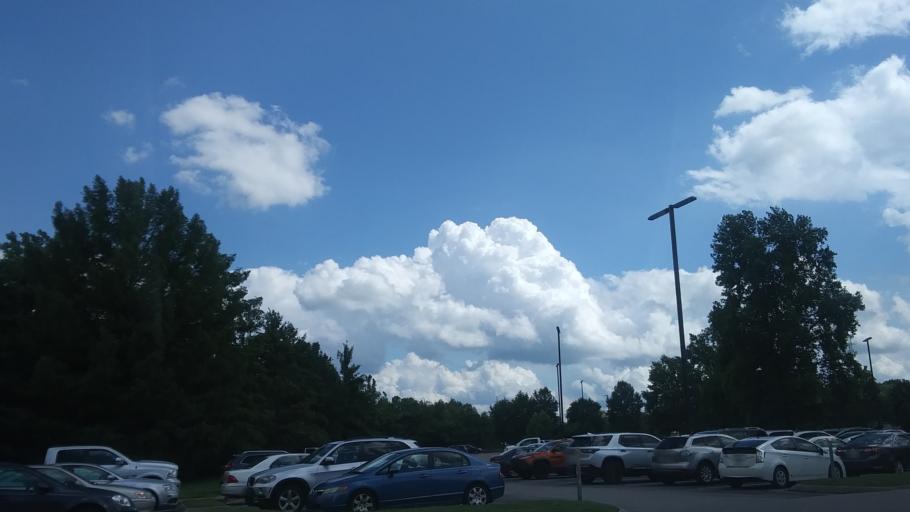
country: US
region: Tennessee
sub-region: Davidson County
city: Oak Hill
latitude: 36.0944
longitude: -86.7009
